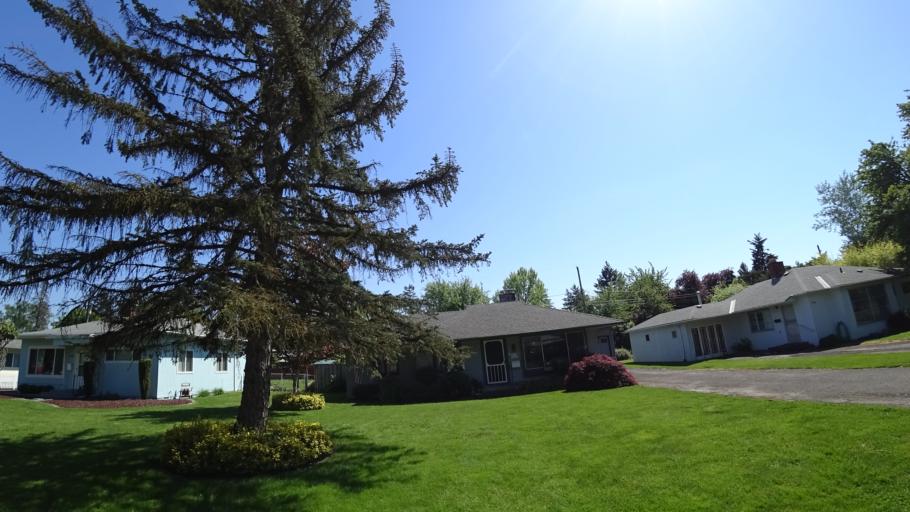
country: US
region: Oregon
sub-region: Washington County
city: Cedar Hills
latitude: 45.4971
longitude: -122.8030
